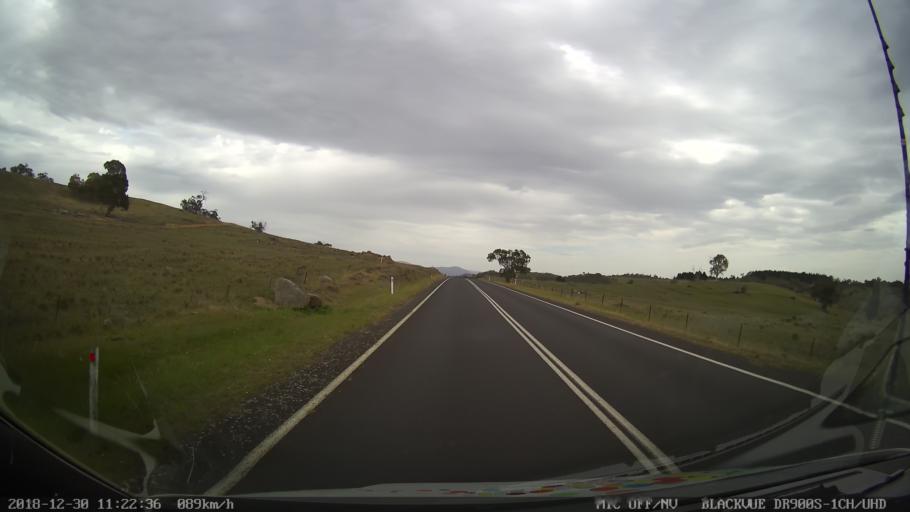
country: AU
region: New South Wales
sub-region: Snowy River
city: Jindabyne
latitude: -36.4982
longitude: 148.6709
